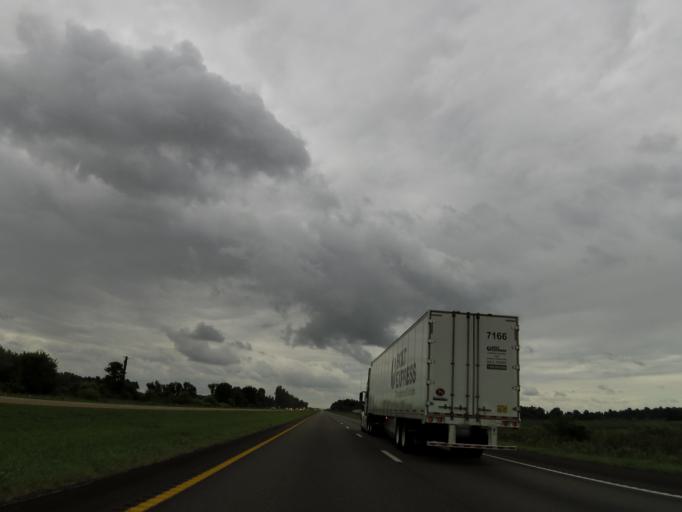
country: US
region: Missouri
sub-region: Mississippi County
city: Charleston
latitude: 36.9063
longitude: -89.4123
